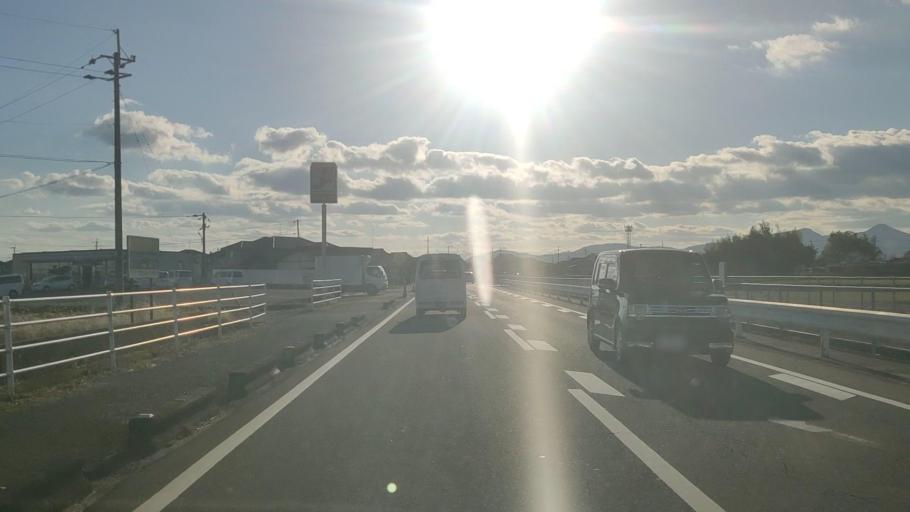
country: JP
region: Saga Prefecture
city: Saga-shi
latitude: 33.2822
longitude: 130.2296
